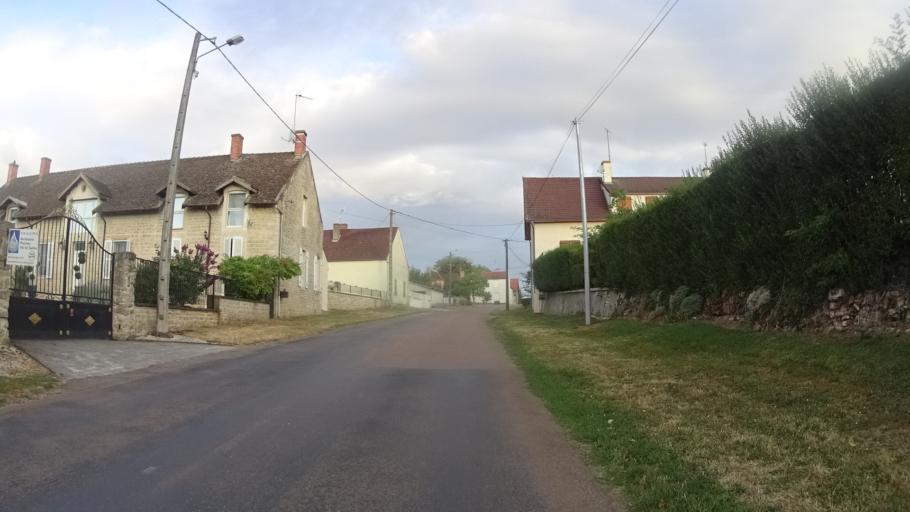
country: FR
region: Bourgogne
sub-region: Departement de la Cote-d'Or
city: Seurre
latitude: 46.9754
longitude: 5.0966
